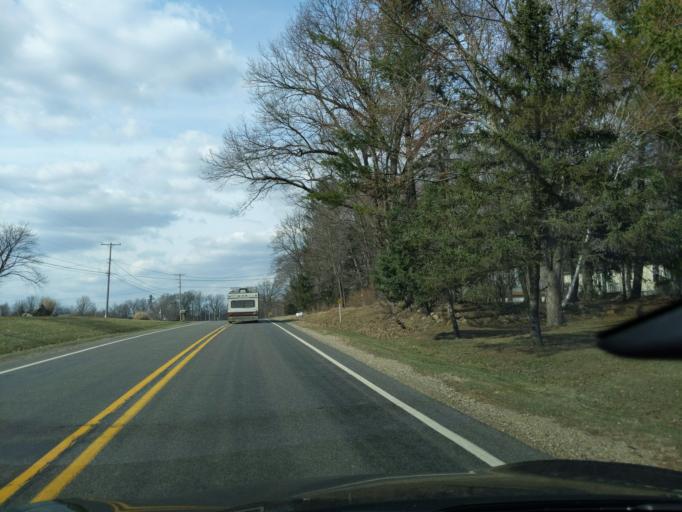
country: US
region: Michigan
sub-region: Ingham County
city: Leslie
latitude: 42.3568
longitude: -84.4183
